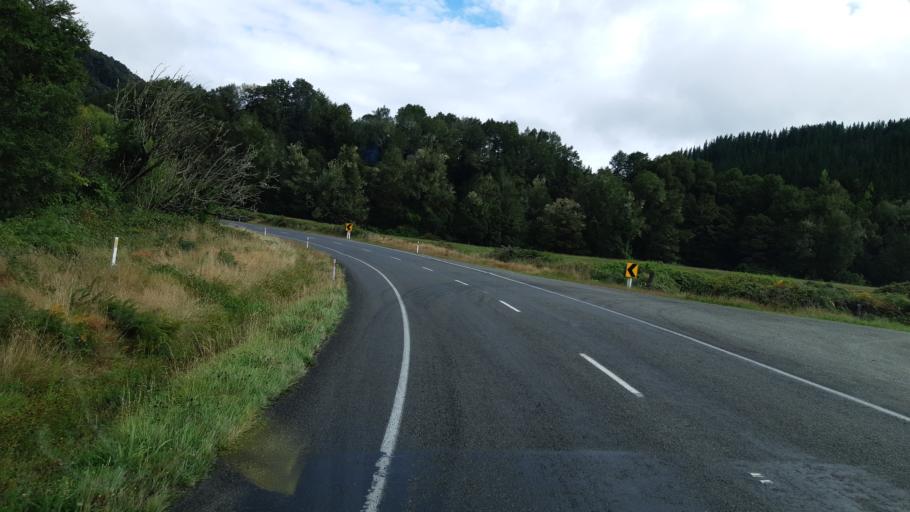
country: NZ
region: West Coast
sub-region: Buller District
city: Westport
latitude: -41.8408
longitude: 172.2469
